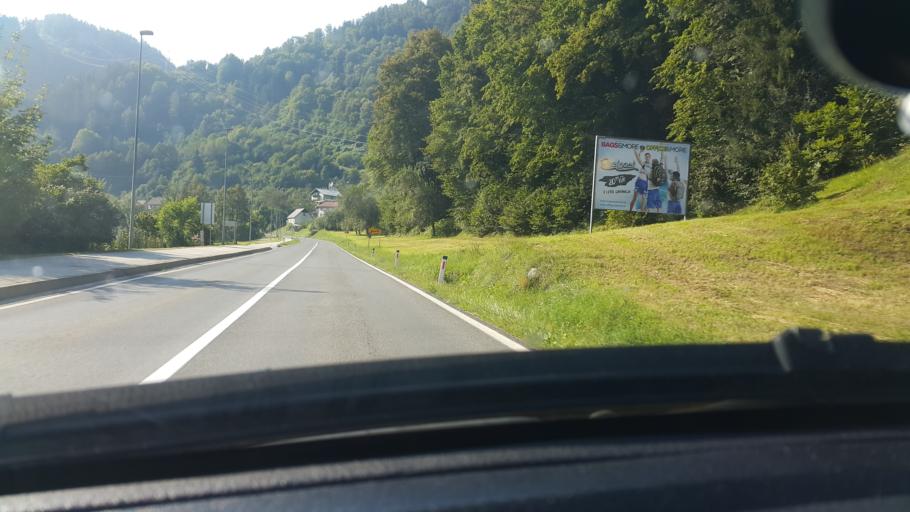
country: SI
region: Podvelka
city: Podvelka
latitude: 46.5966
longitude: 15.3164
